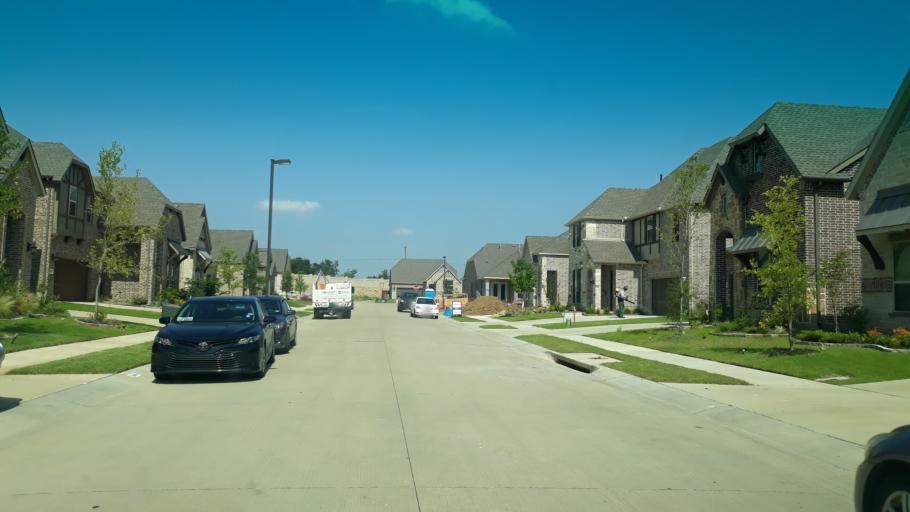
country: US
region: Texas
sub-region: Dallas County
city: Irving
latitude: 32.8701
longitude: -96.9938
